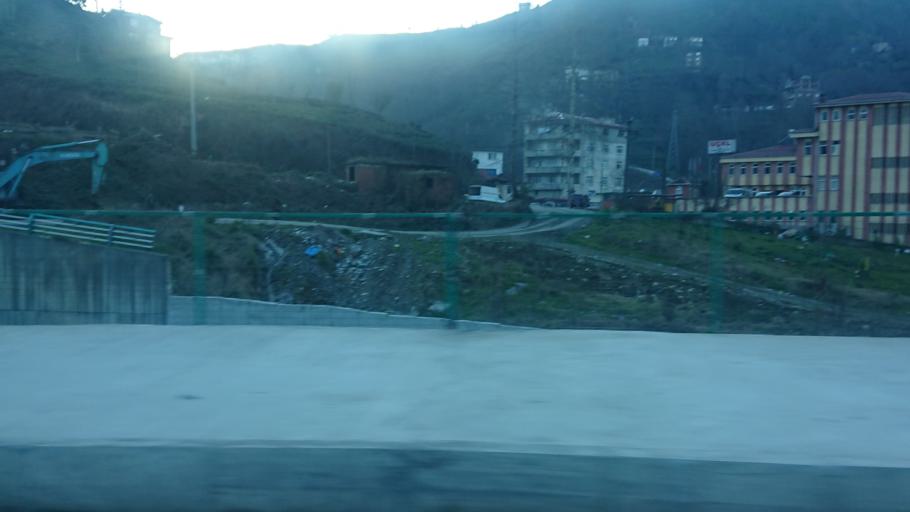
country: TR
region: Rize
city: Gundogdu
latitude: 41.0187
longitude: 40.5774
